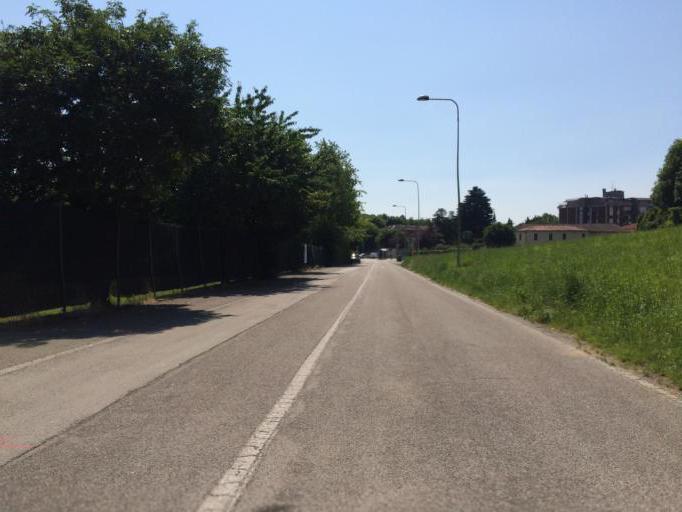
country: IT
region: Veneto
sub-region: Provincia di Vicenza
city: Montegalda
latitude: 45.4460
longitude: 11.6729
